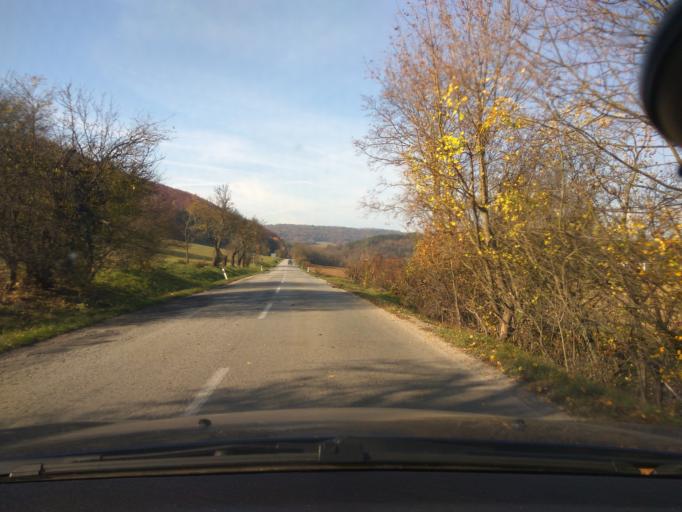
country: SK
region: Nitriansky
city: Brezova pod Bradlom
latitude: 48.6526
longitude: 17.5217
